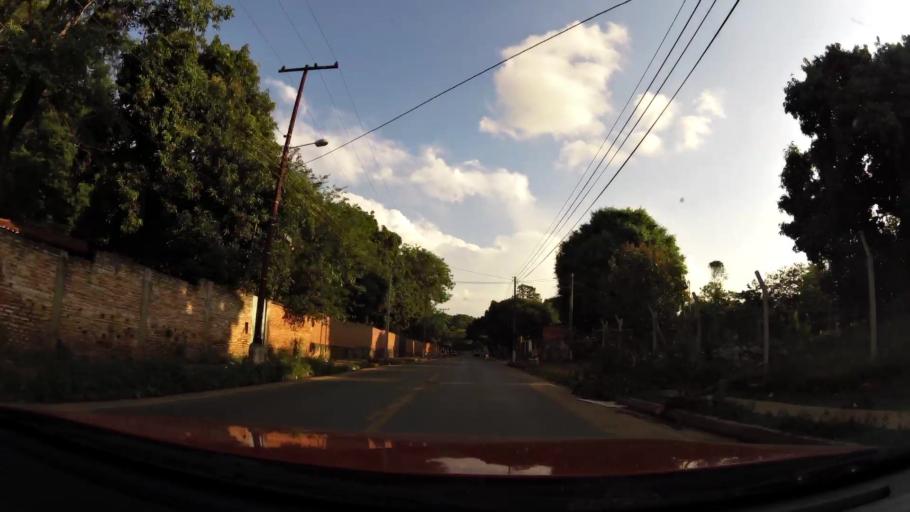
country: PY
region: Central
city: Fernando de la Mora
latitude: -25.3517
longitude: -57.5194
